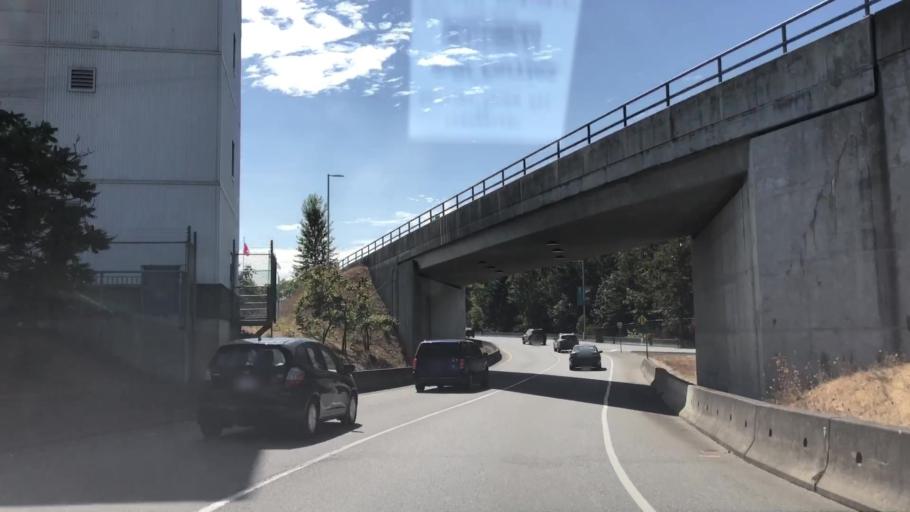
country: CA
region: British Columbia
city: Nanaimo
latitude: 49.1587
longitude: -123.8918
